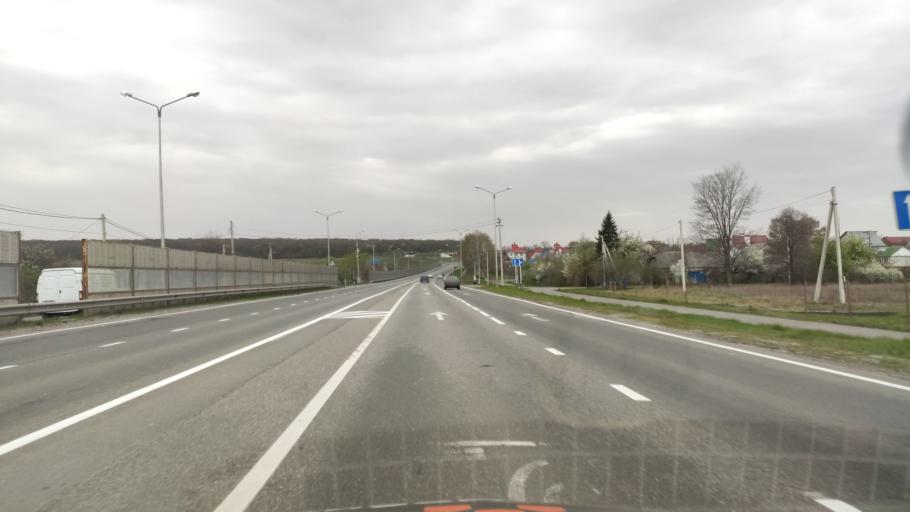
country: RU
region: Belgorod
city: Staryy Oskol
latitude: 51.3423
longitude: 37.8050
